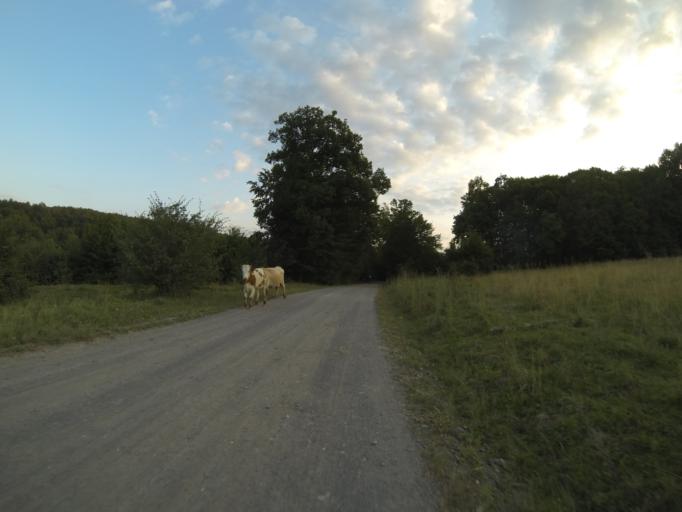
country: RO
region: Brasov
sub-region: Comuna Sinca Noua
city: Sinca Noua
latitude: 45.7380
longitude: 25.2957
